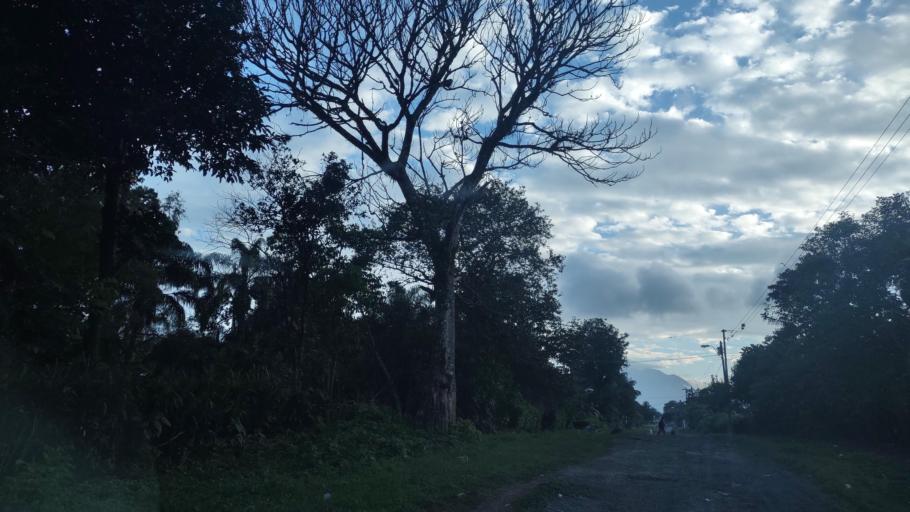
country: MX
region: Veracruz
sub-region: Ixtaczoquitlan
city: Buenavista
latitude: 18.9195
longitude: -97.0455
